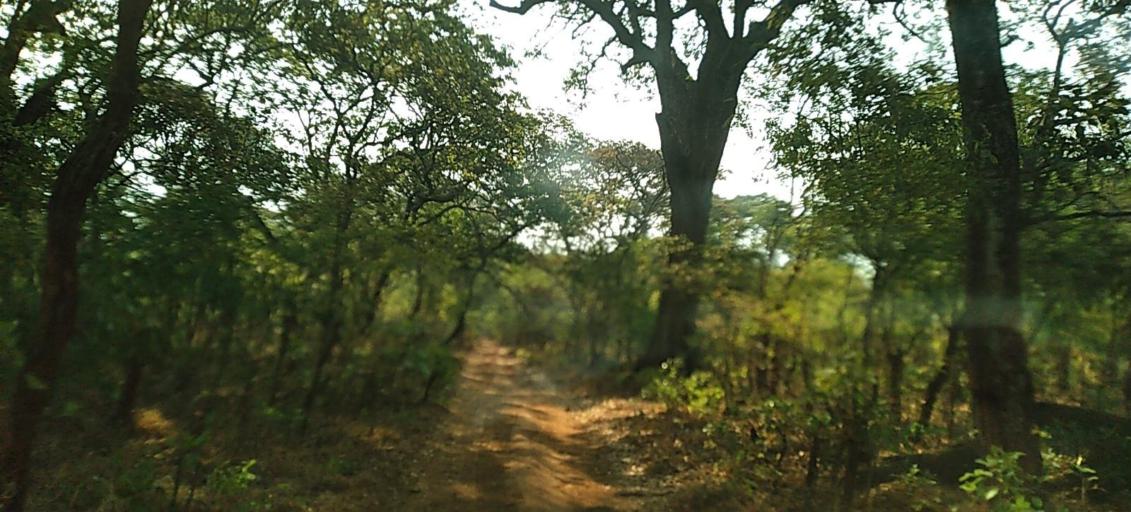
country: ZM
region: North-Western
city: Solwezi
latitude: -12.0608
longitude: 26.1714
